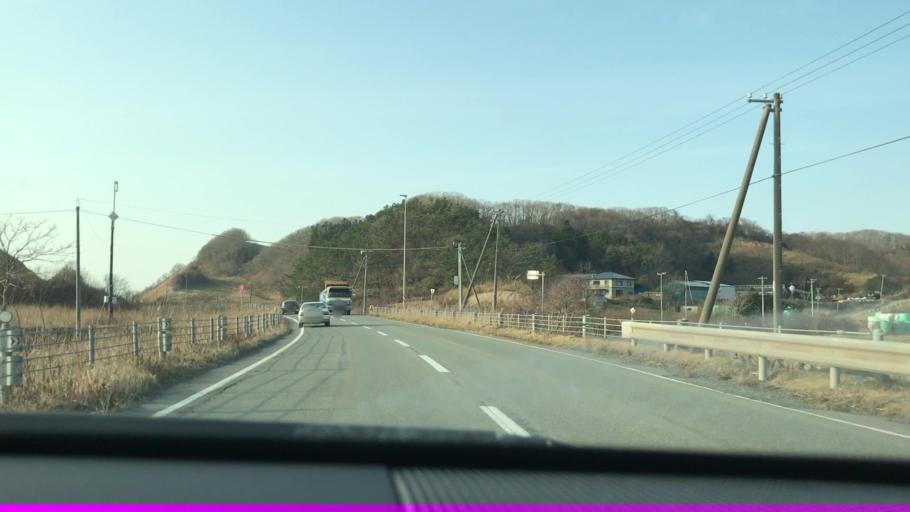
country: JP
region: Hokkaido
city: Shizunai-furukawacho
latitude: 42.2311
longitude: 142.6115
